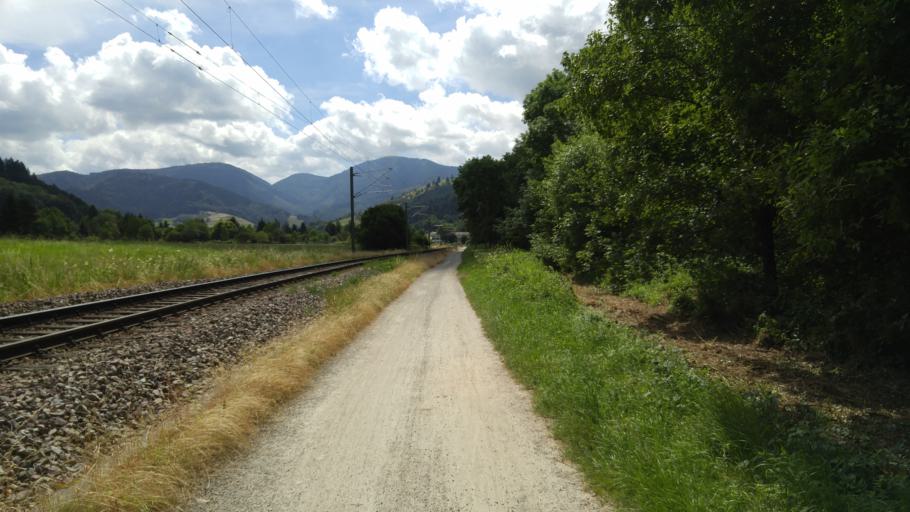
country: DE
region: Baden-Wuerttemberg
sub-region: Freiburg Region
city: Muenstertal/Schwarzwald
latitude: 47.8633
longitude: 7.7560
